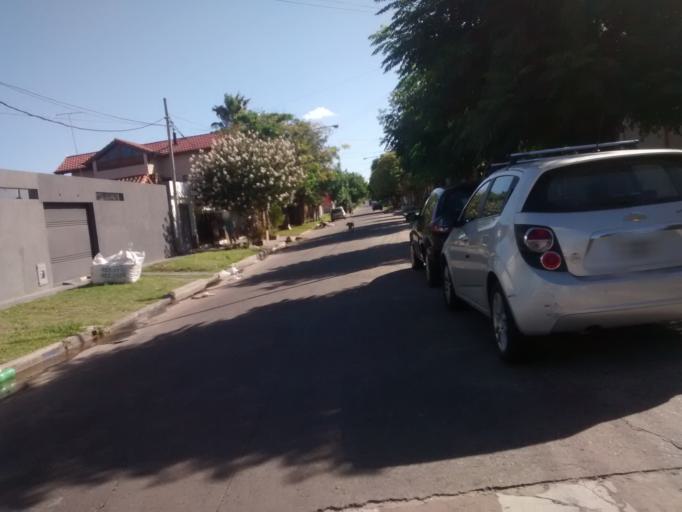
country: AR
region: Buenos Aires
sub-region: Partido de La Plata
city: La Plata
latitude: -34.9228
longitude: -57.9118
